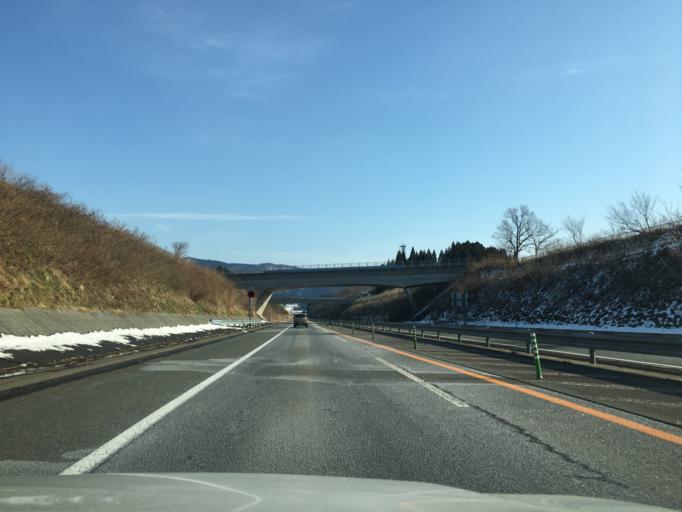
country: JP
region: Yamagata
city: Tsuruoka
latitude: 38.6344
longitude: 139.8327
